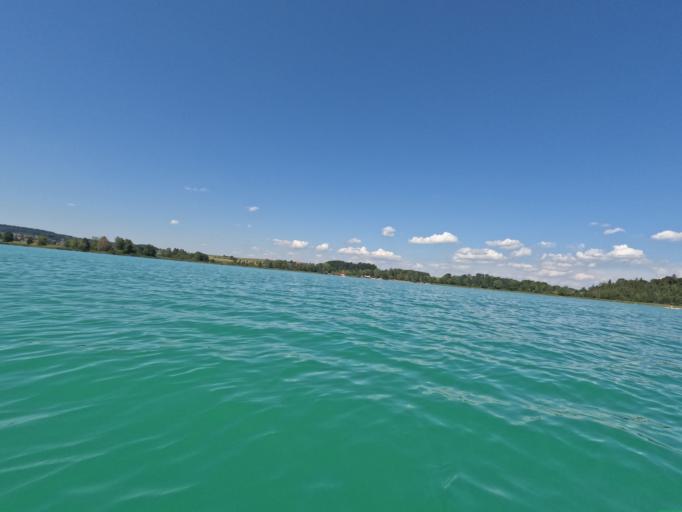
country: DE
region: Bavaria
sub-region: Upper Bavaria
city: Taching am See
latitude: 47.9816
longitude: 12.7447
